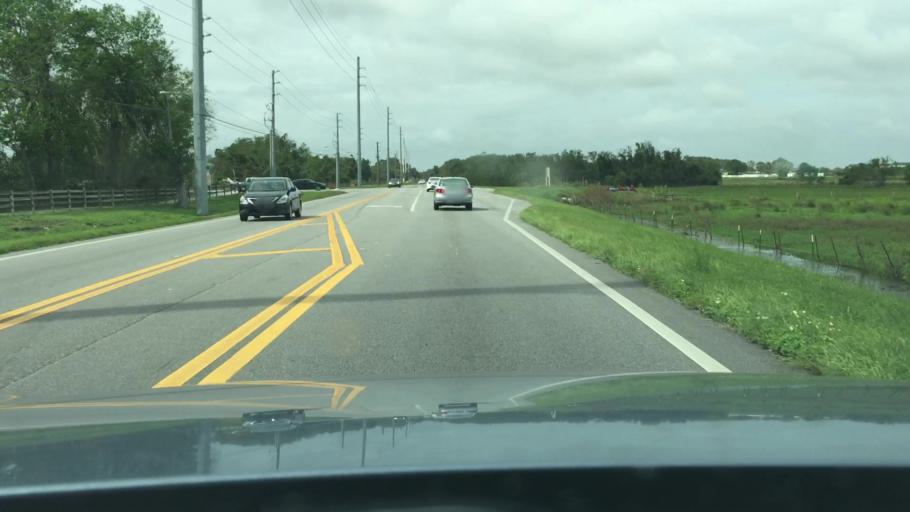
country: US
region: Florida
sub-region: Osceola County
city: Buenaventura Lakes
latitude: 28.2721
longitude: -81.3550
